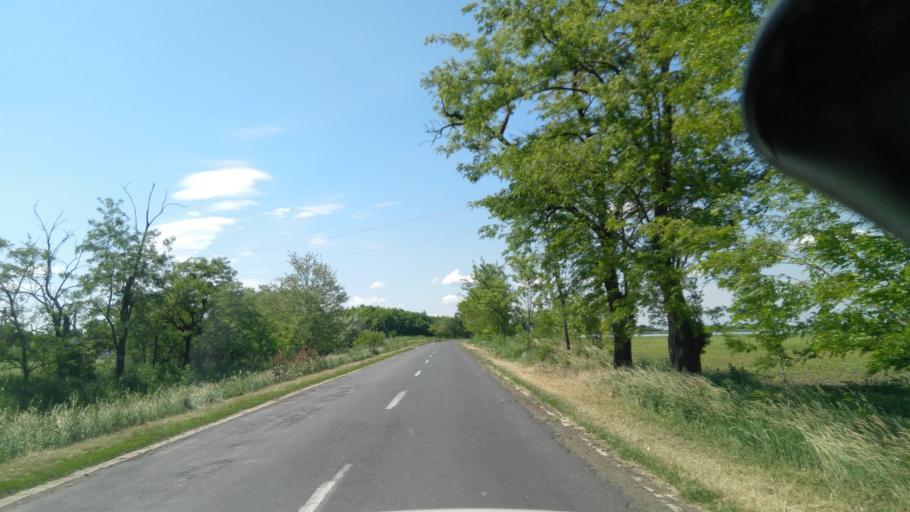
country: HU
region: Bekes
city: Medgyesegyhaza
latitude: 46.4740
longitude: 21.0189
